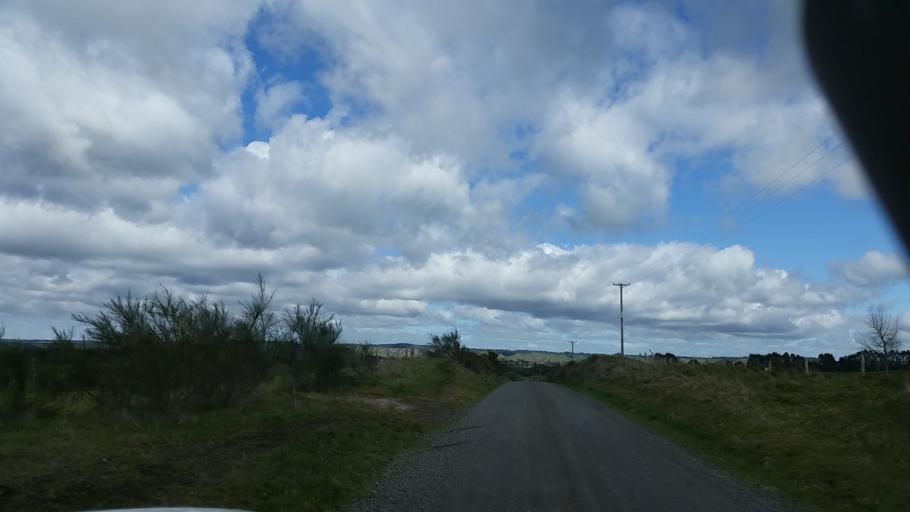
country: NZ
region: Bay of Plenty
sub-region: Whakatane District
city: Murupara
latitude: -38.2982
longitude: 176.5664
